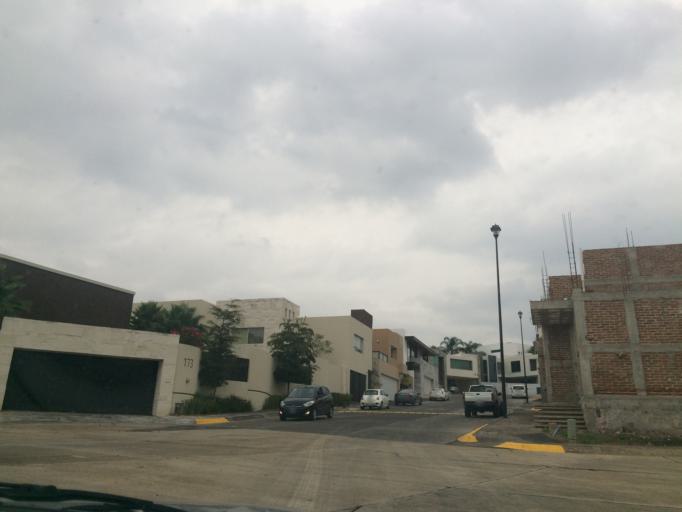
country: MX
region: Guanajuato
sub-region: Leon
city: La Ermita
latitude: 21.1719
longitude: -101.7112
